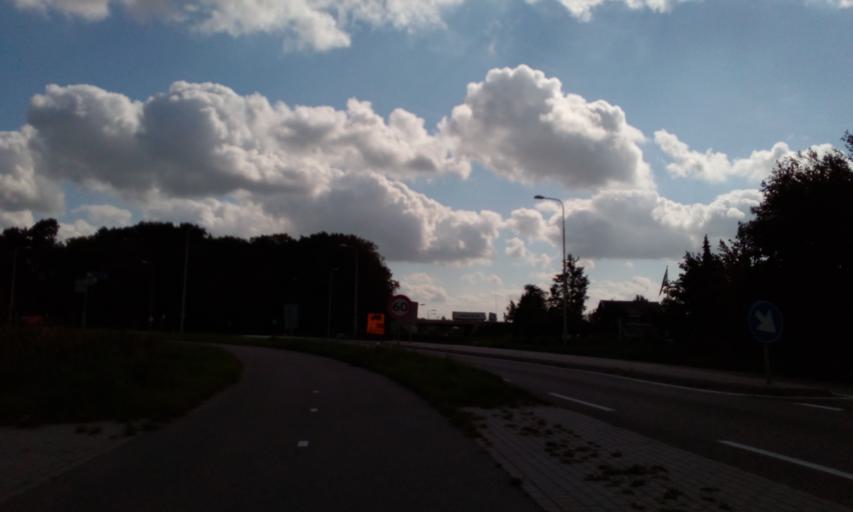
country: NL
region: South Holland
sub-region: Gemeente Waddinxveen
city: Waddinxveen
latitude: 52.0009
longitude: 4.6475
